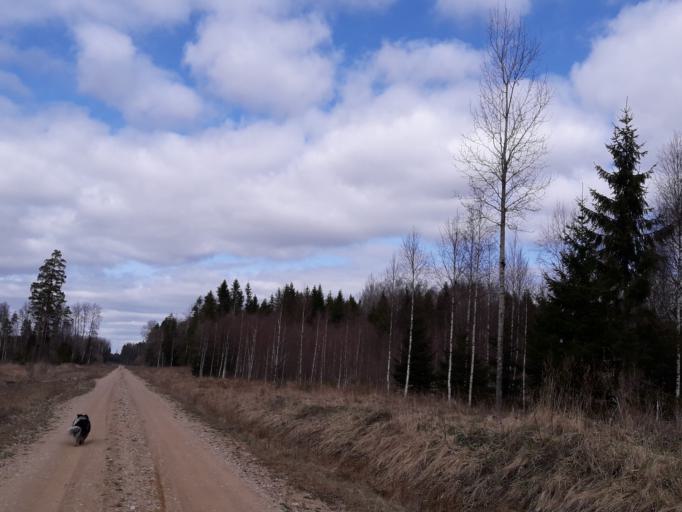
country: LV
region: Talsu Rajons
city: Sabile
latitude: 56.8951
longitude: 22.3794
